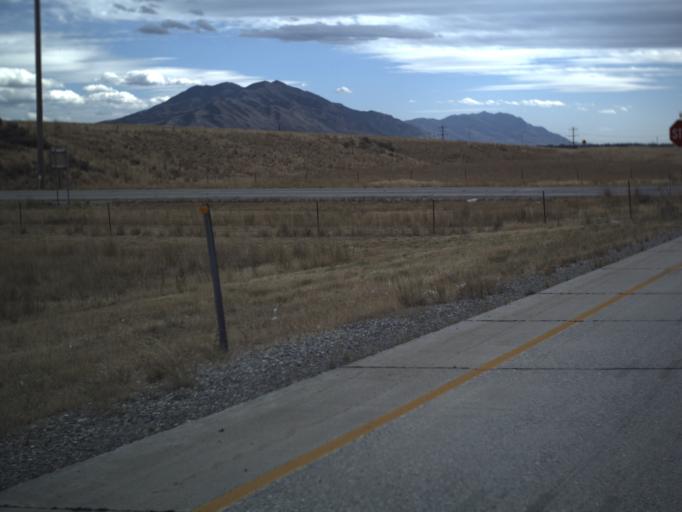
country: US
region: Utah
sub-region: Box Elder County
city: Garland
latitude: 41.8872
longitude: -112.1717
